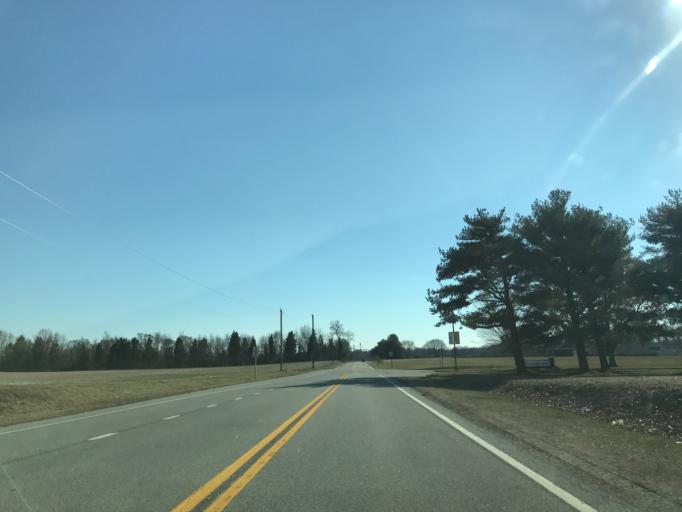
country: US
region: Maryland
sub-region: Queen Anne's County
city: Centreville
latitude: 38.9528
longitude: -76.0786
